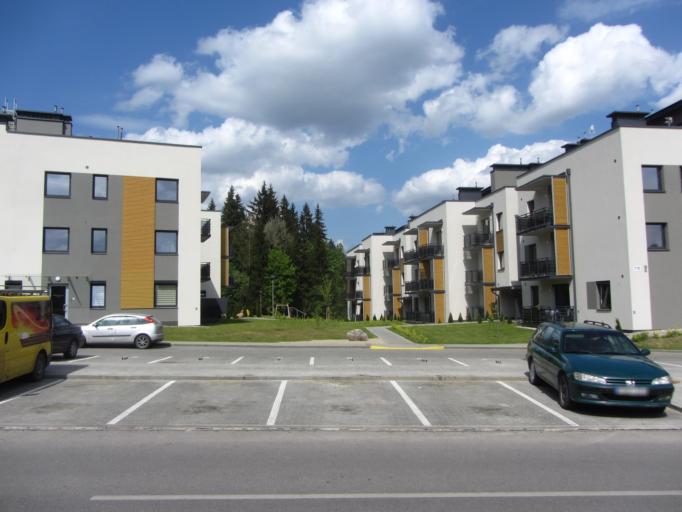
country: LT
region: Vilnius County
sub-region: Vilnius
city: Fabijoniskes
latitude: 54.7650
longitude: 25.2834
